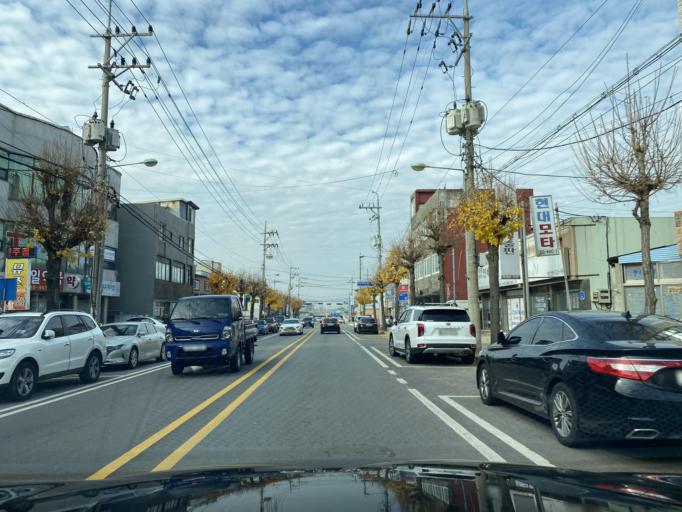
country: KR
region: Chungcheongnam-do
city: Yesan
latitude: 36.6821
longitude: 126.8310
